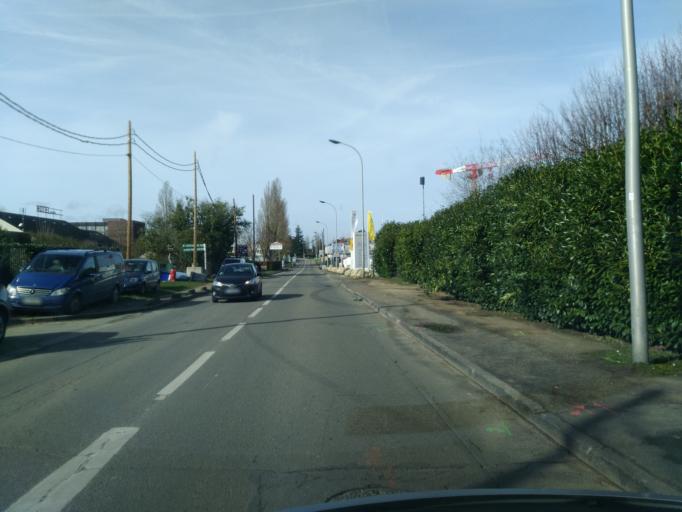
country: FR
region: Ile-de-France
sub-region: Departement des Yvelines
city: Les Clayes-sous-Bois
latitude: 48.8019
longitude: 1.9789
